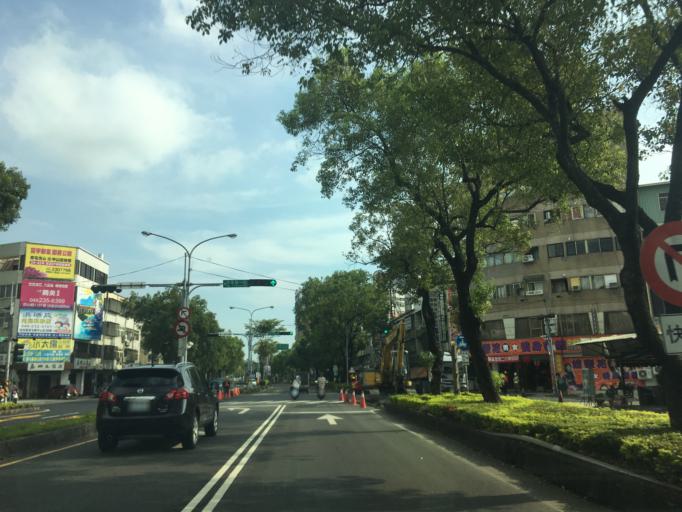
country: TW
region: Taiwan
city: Zhongxing New Village
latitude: 23.9848
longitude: 120.6823
